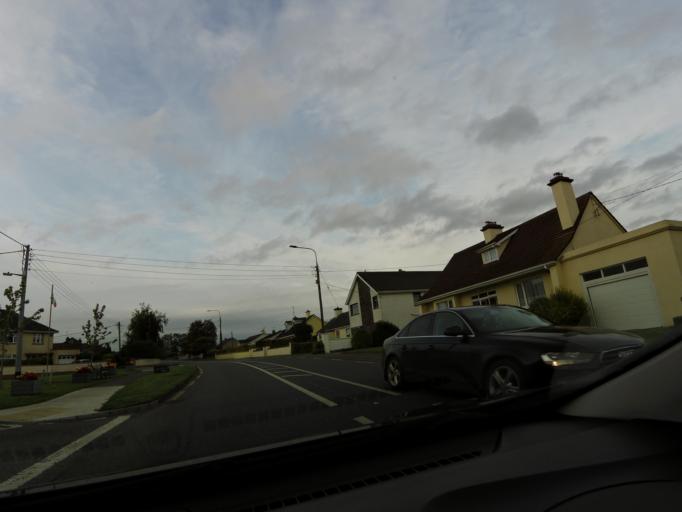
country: IE
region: Leinster
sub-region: Uibh Fhaili
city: Ferbane
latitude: 53.2744
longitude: -7.8268
